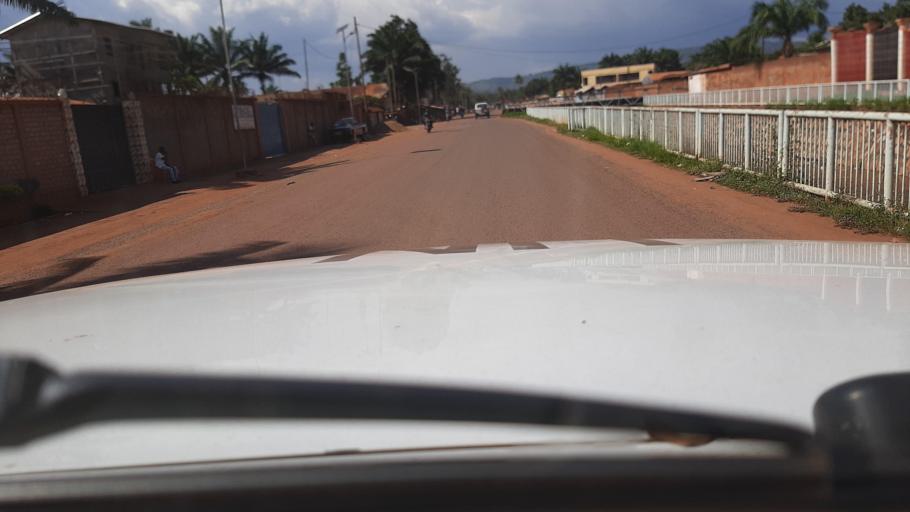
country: CF
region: Bangui
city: Bangui
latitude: 4.3751
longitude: 18.5531
